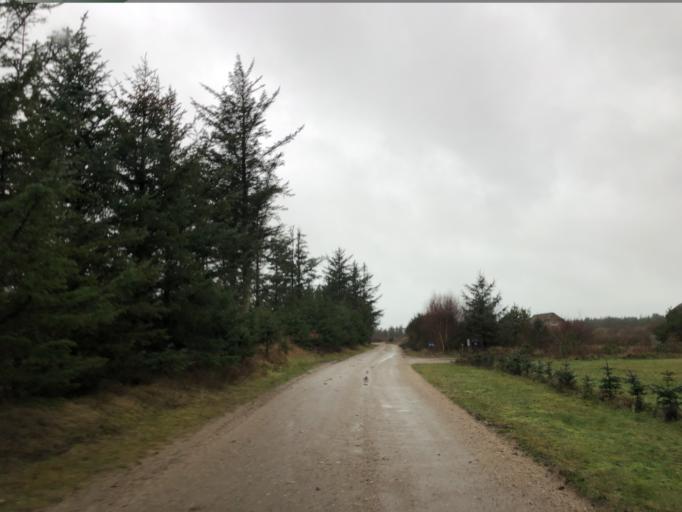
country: DK
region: Central Jutland
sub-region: Holstebro Kommune
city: Ulfborg
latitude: 56.2788
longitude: 8.1465
